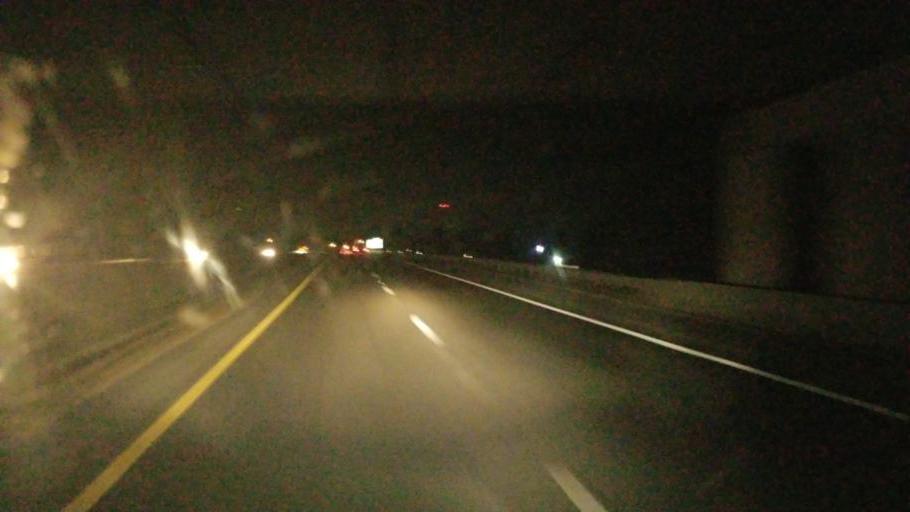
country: US
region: Ohio
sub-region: Belmont County
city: Saint Clairsville
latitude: 40.0778
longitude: -80.9449
